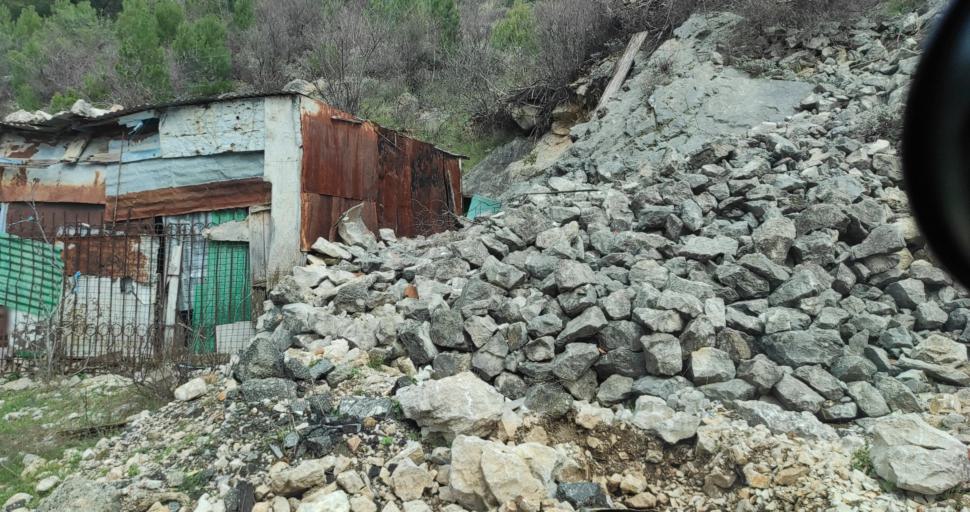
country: AL
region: Lezhe
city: Shengjin
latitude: 41.8164
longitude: 19.5893
